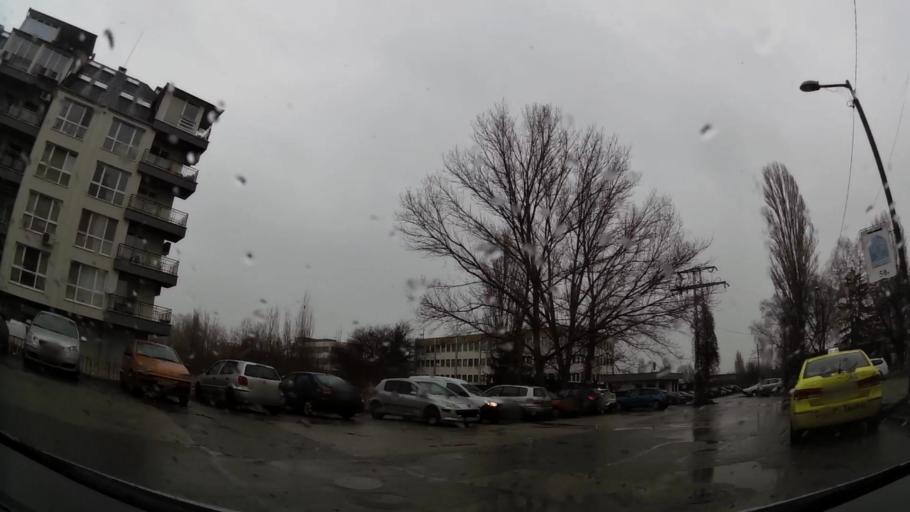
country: BG
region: Sofia-Capital
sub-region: Stolichna Obshtina
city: Sofia
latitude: 42.6659
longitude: 23.3804
